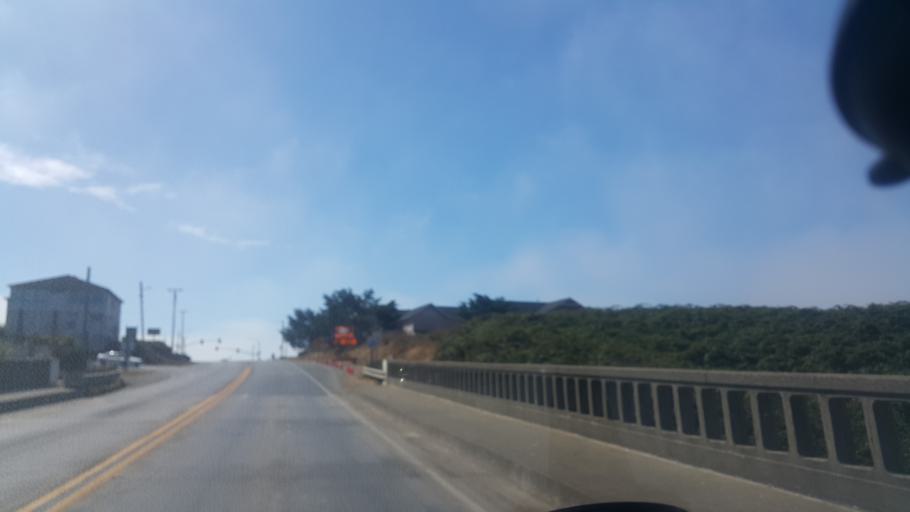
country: US
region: California
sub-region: Mendocino County
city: Fort Bragg
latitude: 39.4538
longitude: -123.8058
